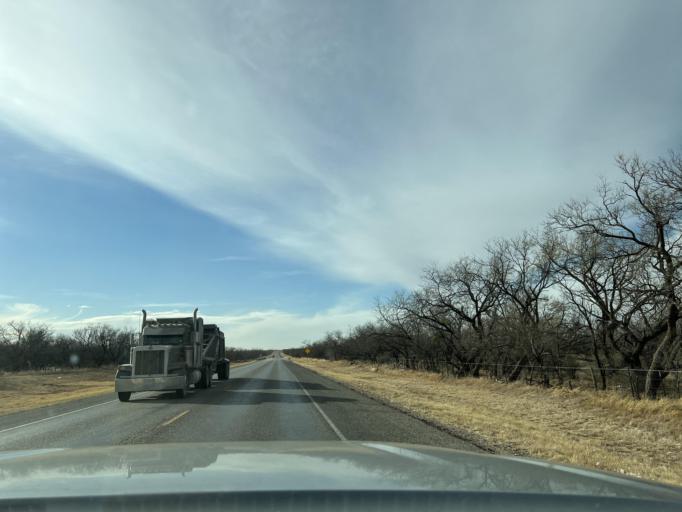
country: US
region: Texas
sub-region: Fisher County
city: Rotan
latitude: 32.7399
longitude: -100.5099
